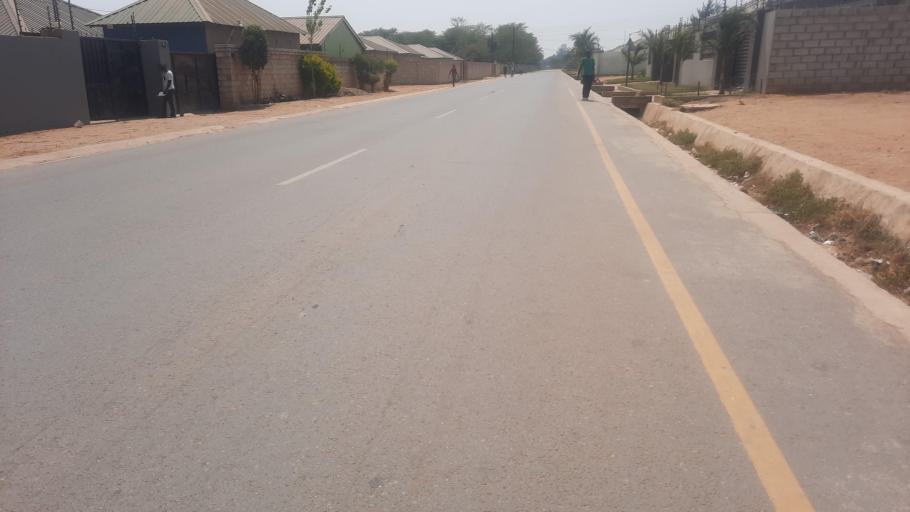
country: ZM
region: Lusaka
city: Lusaka
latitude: -15.3916
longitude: 28.3900
